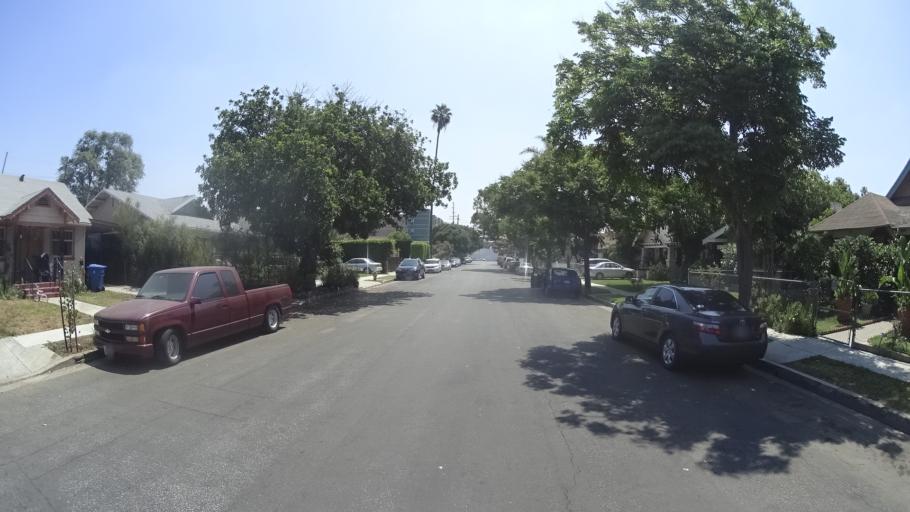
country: US
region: California
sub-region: Los Angeles County
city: View Park-Windsor Hills
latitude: 34.0265
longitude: -118.3109
